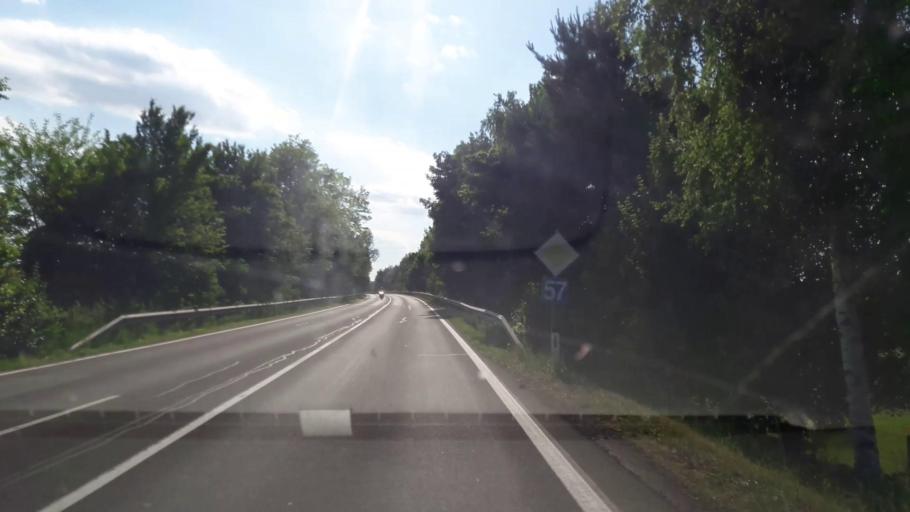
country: AT
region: Styria
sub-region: Politischer Bezirk Suedoststeiermark
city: Fehring
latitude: 46.9431
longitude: 16.0162
